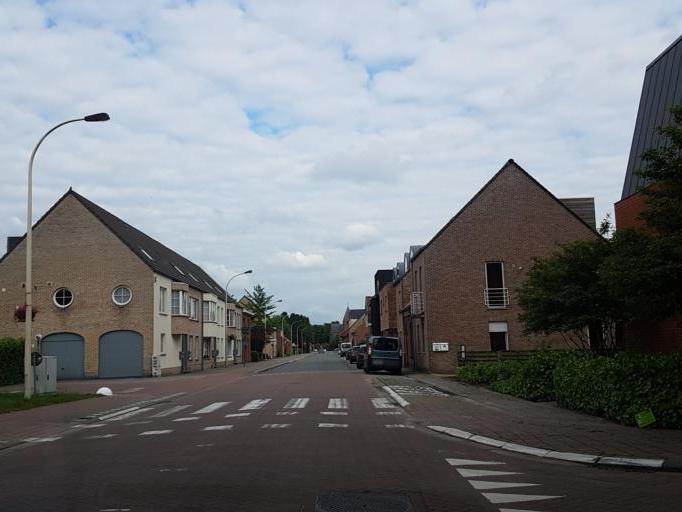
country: BE
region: Flanders
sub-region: Provincie Antwerpen
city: Zoersel
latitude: 51.2683
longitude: 4.7058
